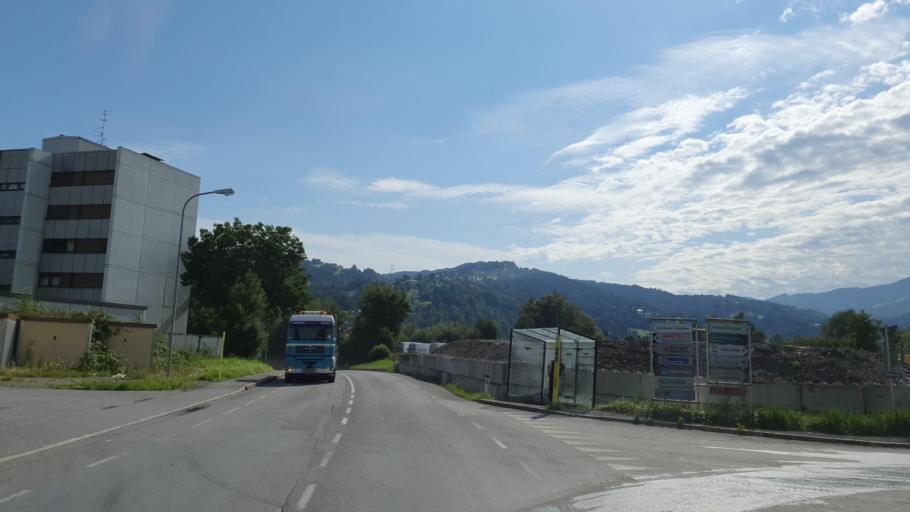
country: AT
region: Vorarlberg
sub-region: Politischer Bezirk Bregenz
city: Wolfurt
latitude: 47.4551
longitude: 9.7408
